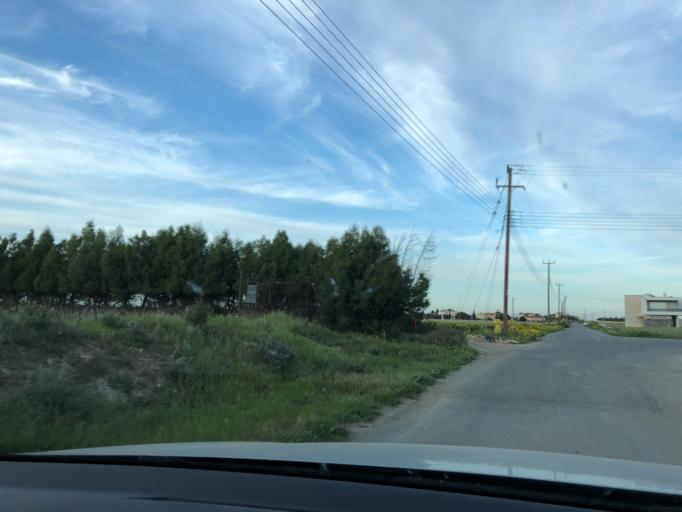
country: CY
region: Larnaka
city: Perivolia
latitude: 34.8343
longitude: 33.5964
